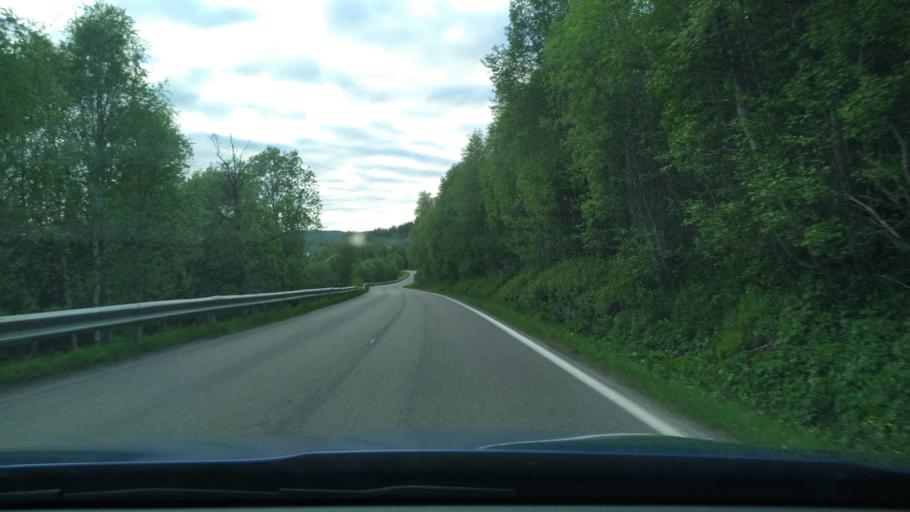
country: NO
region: Troms
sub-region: Sorreisa
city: Sorreisa
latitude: 69.0844
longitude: 18.3581
